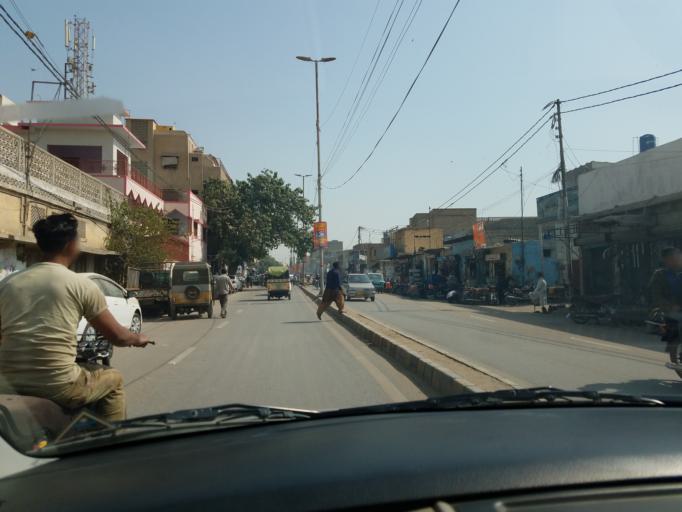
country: PK
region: Sindh
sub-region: Karachi District
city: Karachi
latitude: 24.8913
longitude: 67.0485
